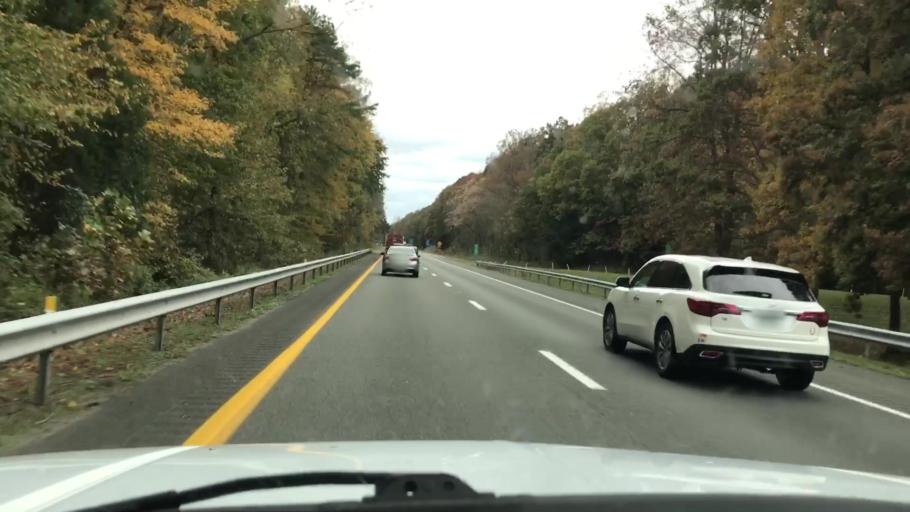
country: US
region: Virginia
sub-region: Goochland County
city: Goochland
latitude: 37.7056
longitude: -77.7651
